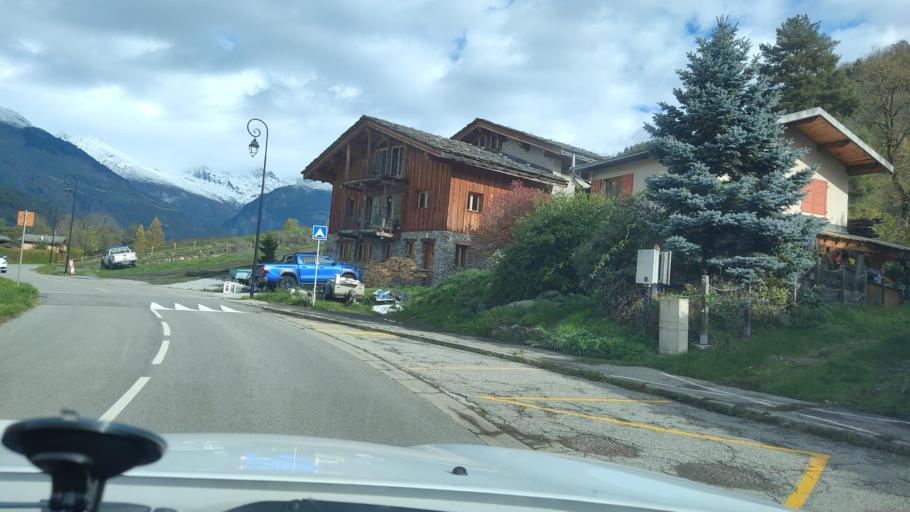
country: FR
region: Rhone-Alpes
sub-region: Departement de la Savoie
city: Bourg-Saint-Maurice
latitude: 45.5821
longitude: 6.7494
